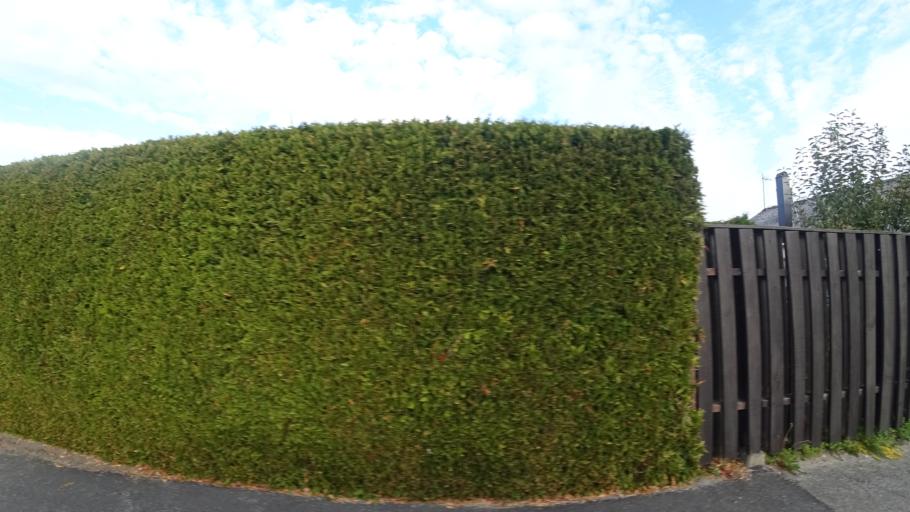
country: SE
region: Skane
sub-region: Staffanstorps Kommun
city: Staffanstorp
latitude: 55.6428
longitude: 13.1925
